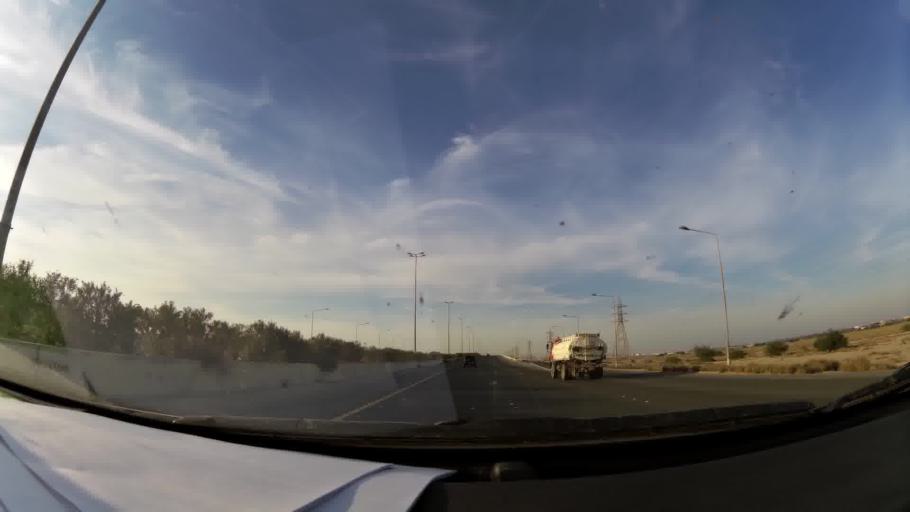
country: KW
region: Al Ahmadi
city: Al Fahahil
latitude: 28.9621
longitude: 48.1667
